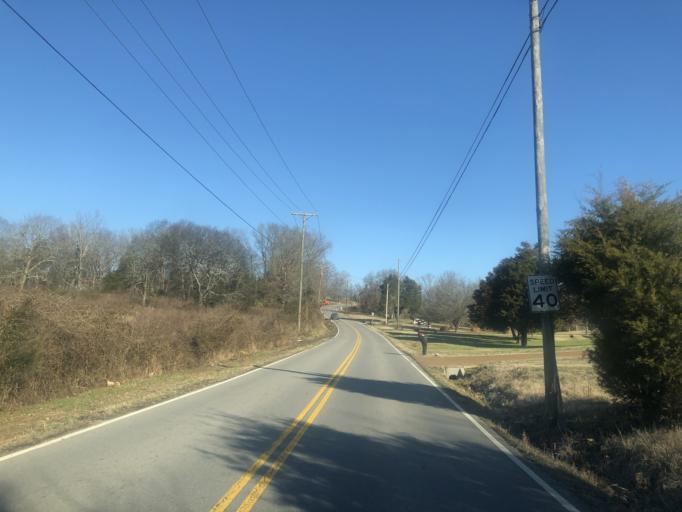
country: US
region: Tennessee
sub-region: Williamson County
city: Nolensville
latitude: 36.0118
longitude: -86.6653
